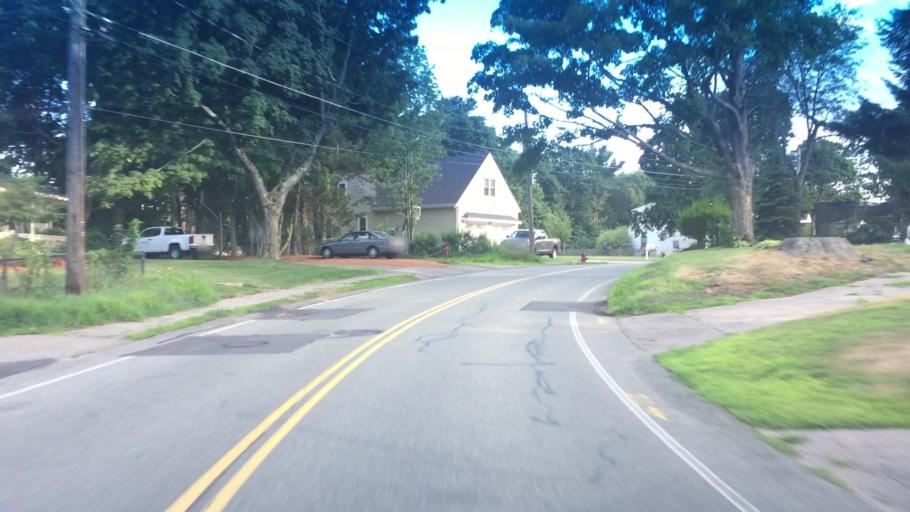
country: US
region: Massachusetts
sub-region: Norfolk County
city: Walpole
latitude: 42.1589
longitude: -71.2222
